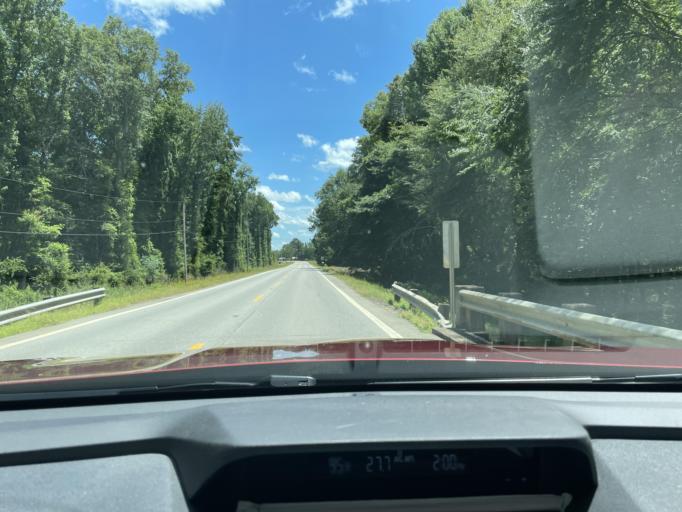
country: US
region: Arkansas
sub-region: Drew County
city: Monticello
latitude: 33.6084
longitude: -91.7374
